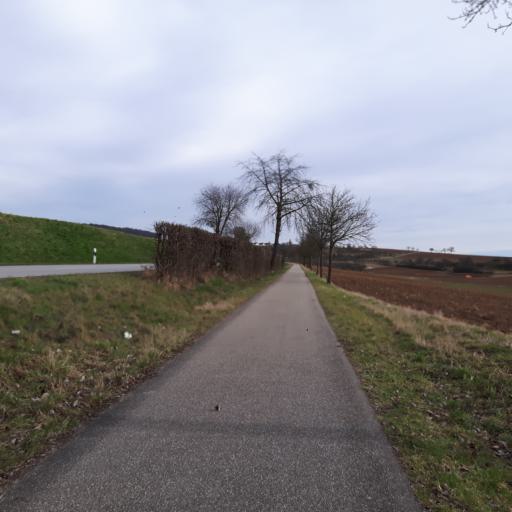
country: DE
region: Baden-Wuerttemberg
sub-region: Regierungsbezirk Stuttgart
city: Abstatt
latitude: 49.0509
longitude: 9.2852
